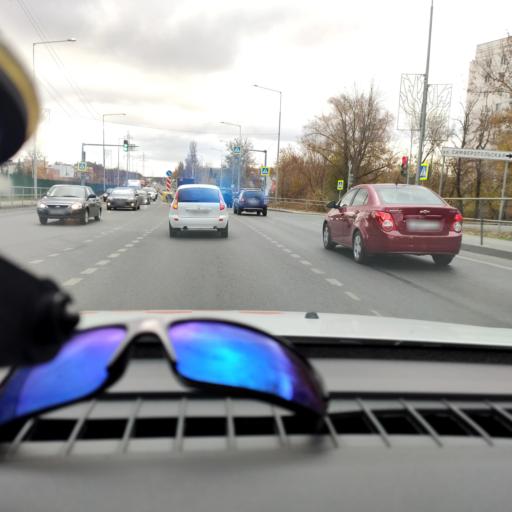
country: RU
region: Samara
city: Volzhskiy
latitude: 53.3515
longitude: 50.2156
